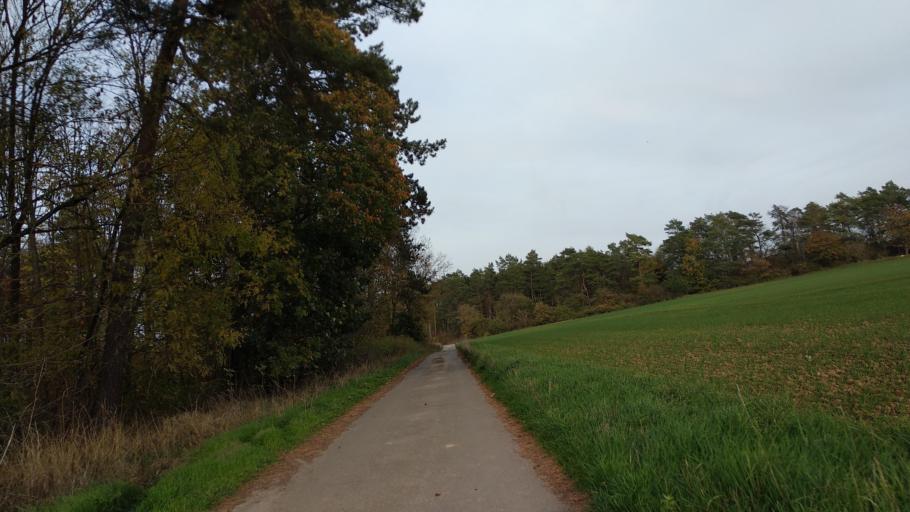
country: DE
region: North Rhine-Westphalia
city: Beverungen
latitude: 51.6905
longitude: 9.3331
